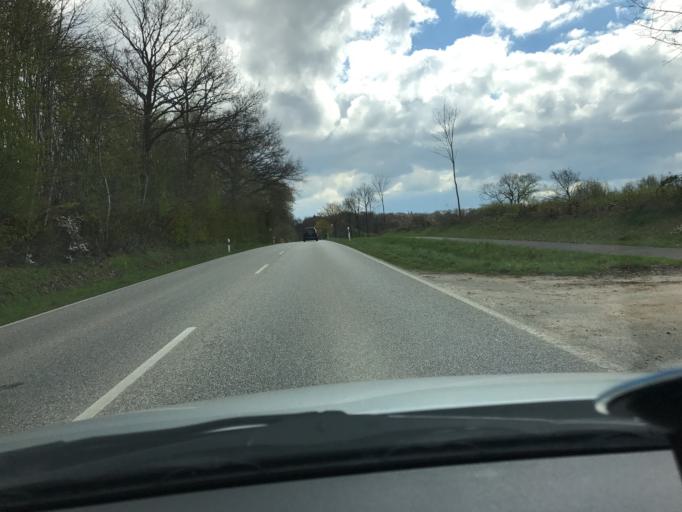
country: DE
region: Schleswig-Holstein
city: Dornick
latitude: 54.1909
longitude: 10.3609
